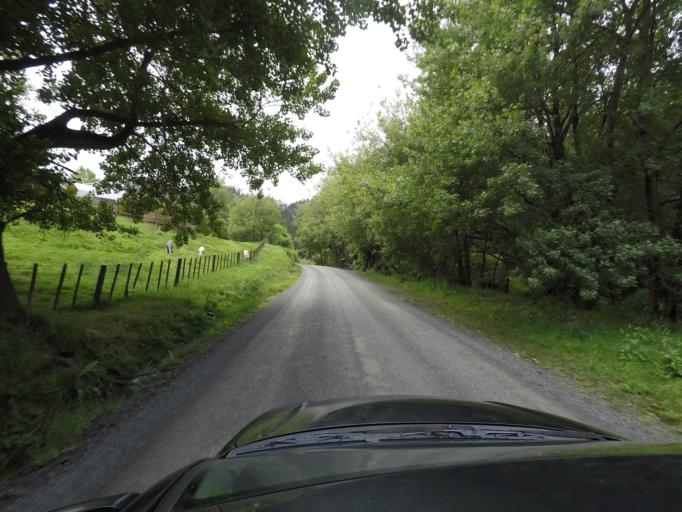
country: NZ
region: Auckland
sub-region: Auckland
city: Warkworth
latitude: -36.4914
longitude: 174.6214
